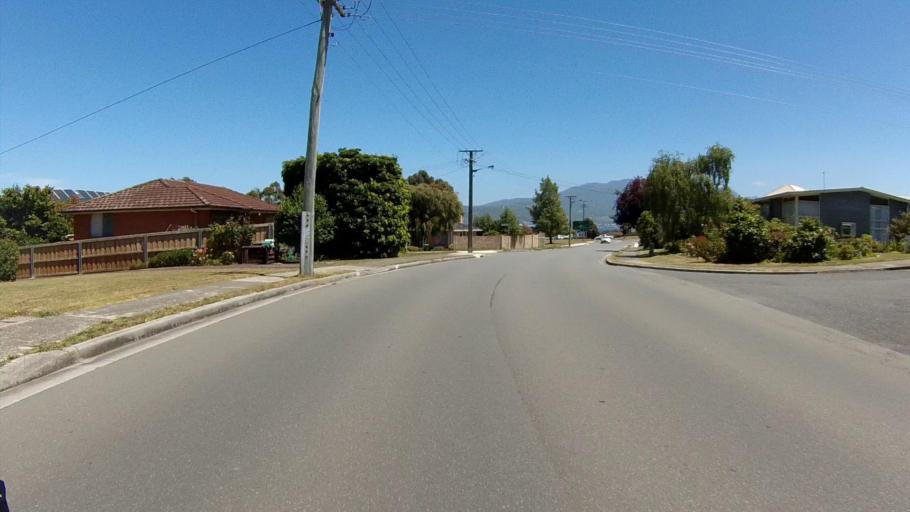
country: AU
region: Tasmania
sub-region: Clarence
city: Howrah
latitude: -42.8779
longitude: 147.4087
